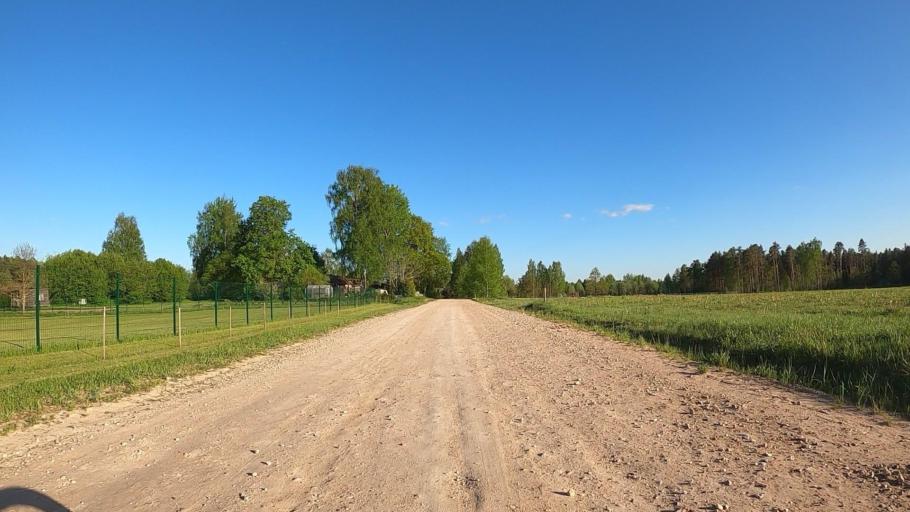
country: LV
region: Kekava
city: Kekava
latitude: 56.7645
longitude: 24.2904
